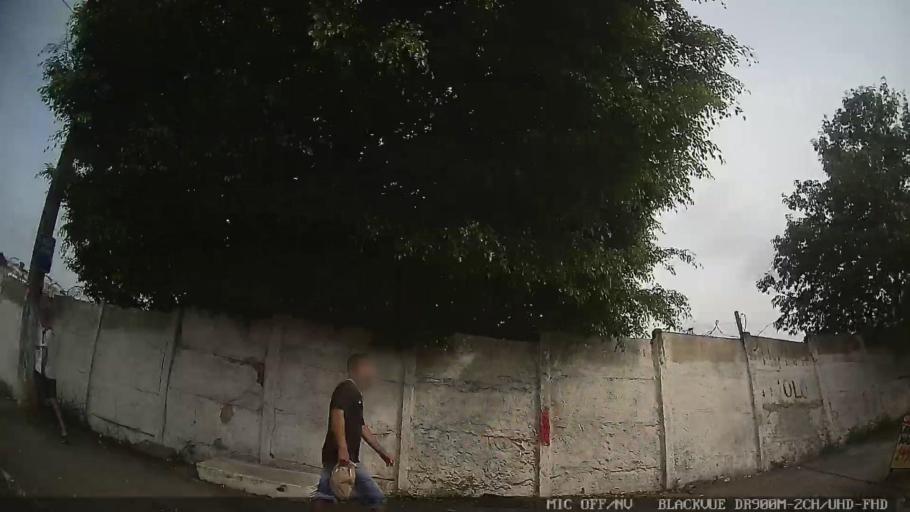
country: BR
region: Sao Paulo
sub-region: Itaquaquecetuba
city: Itaquaquecetuba
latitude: -23.4972
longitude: -46.3673
